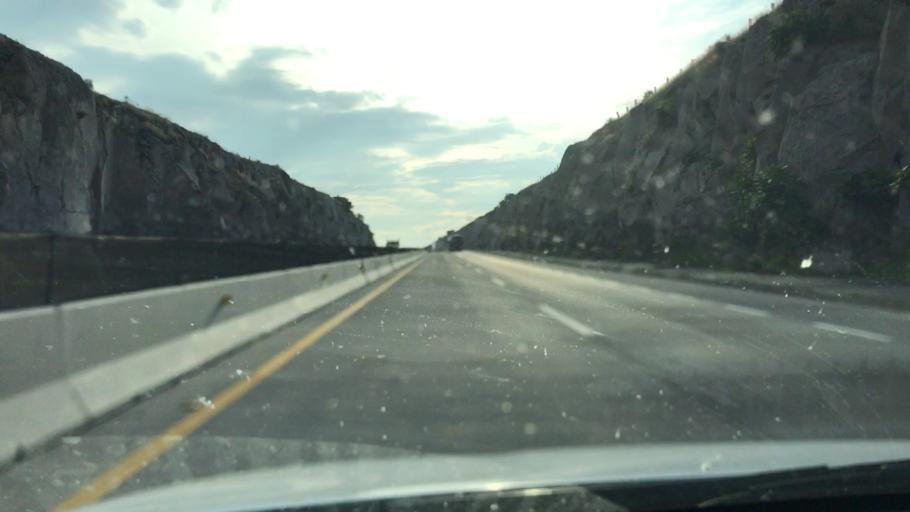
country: MX
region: Guanajuato
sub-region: Penjamo
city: Estacion la Piedad
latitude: 20.4030
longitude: -102.0231
